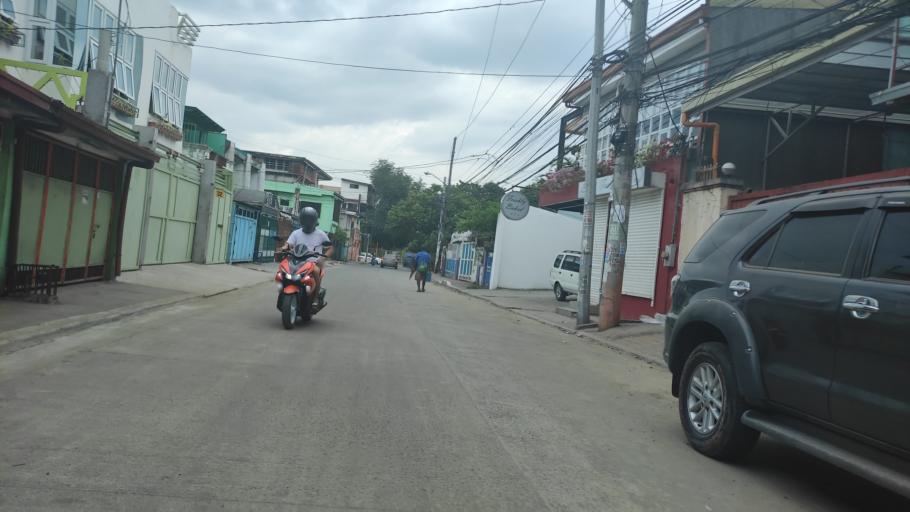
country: PH
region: Calabarzon
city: Bagong Pagasa
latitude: 14.6730
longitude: 121.0184
